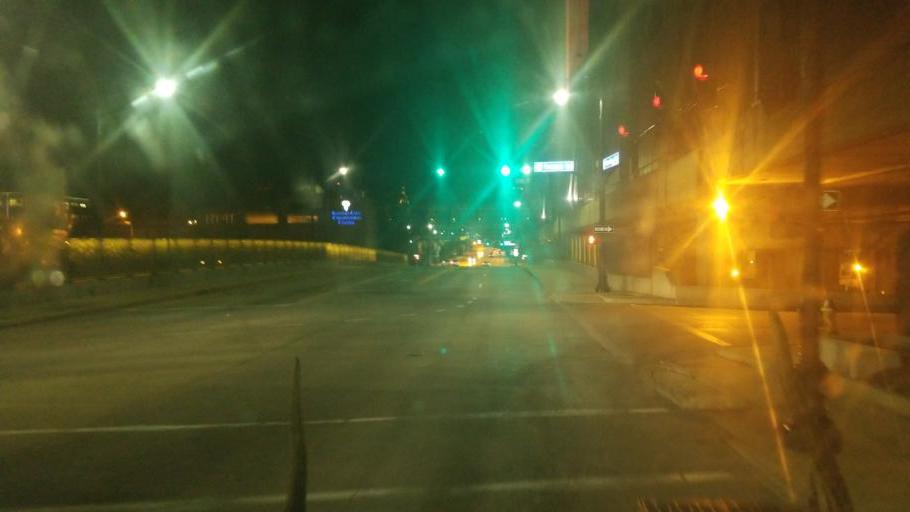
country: US
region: Missouri
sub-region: Jackson County
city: Kansas City
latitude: 39.0956
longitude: -94.5885
